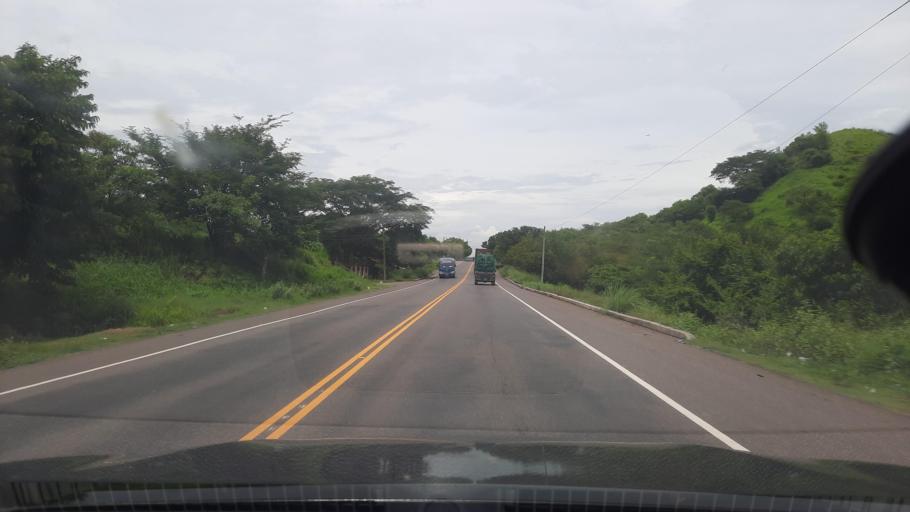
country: HN
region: Valle
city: Goascoran
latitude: 13.5477
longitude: -87.6403
